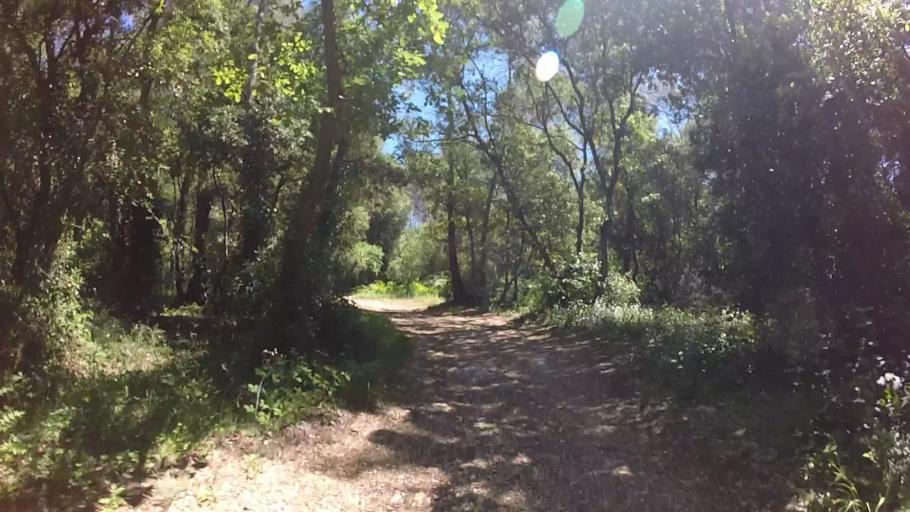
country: FR
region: Provence-Alpes-Cote d'Azur
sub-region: Departement des Alpes-Maritimes
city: Valbonne
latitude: 43.6245
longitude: 7.0165
